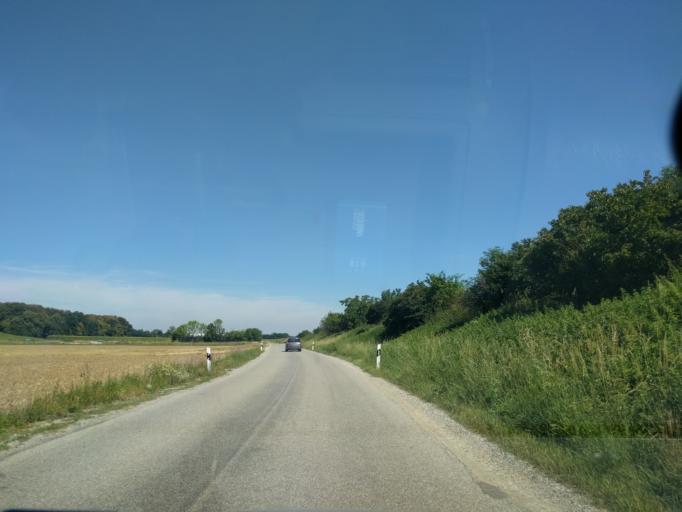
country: DE
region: Bavaria
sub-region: Upper Bavaria
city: Fuerstenfeldbruck
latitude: 48.1904
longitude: 11.2275
